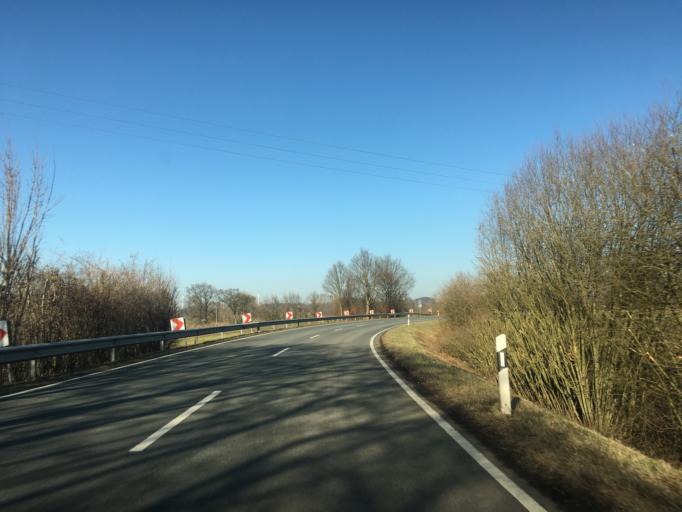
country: DE
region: North Rhine-Westphalia
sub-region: Regierungsbezirk Munster
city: Horstmar
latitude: 52.0591
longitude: 7.2771
